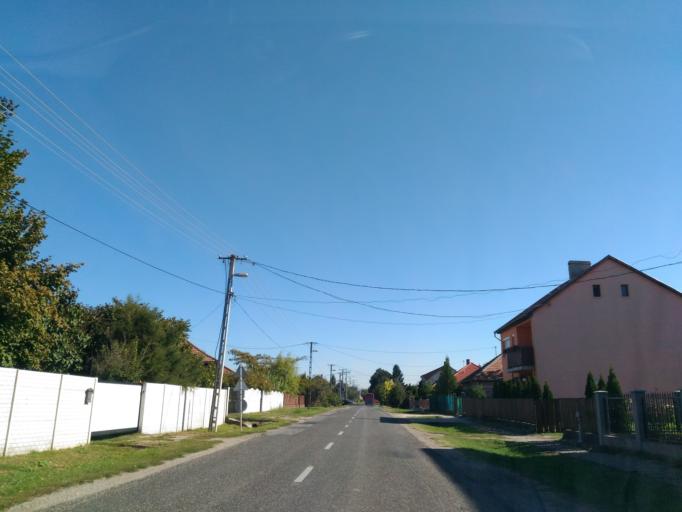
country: HU
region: Fejer
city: Ivancsa
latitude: 47.1555
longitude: 18.8231
